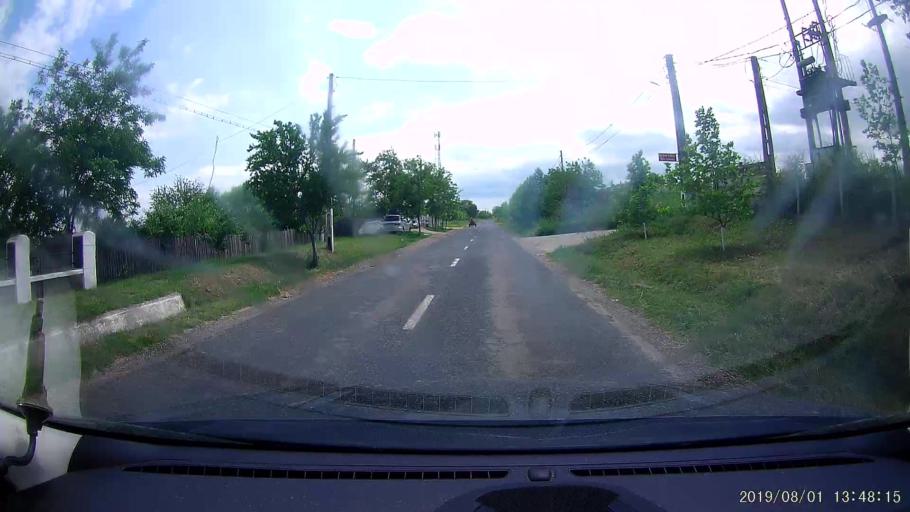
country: RO
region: Galati
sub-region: Comuna Oancea
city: Oancea
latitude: 45.9101
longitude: 28.1121
